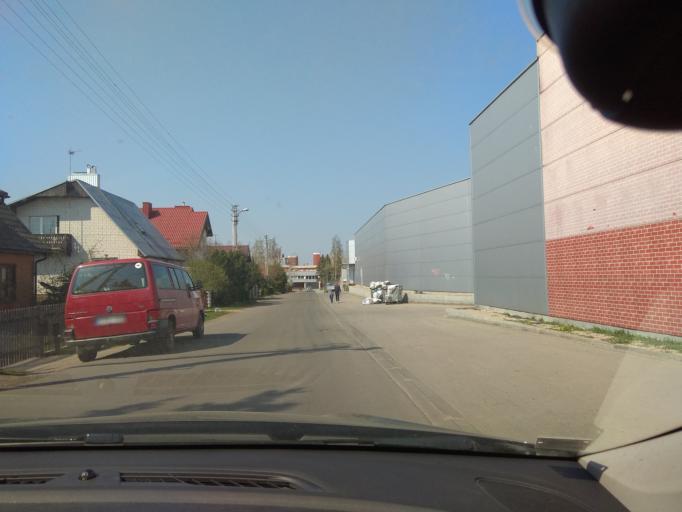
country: LT
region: Marijampoles apskritis
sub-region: Marijampole Municipality
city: Marijampole
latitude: 54.5663
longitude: 23.3500
